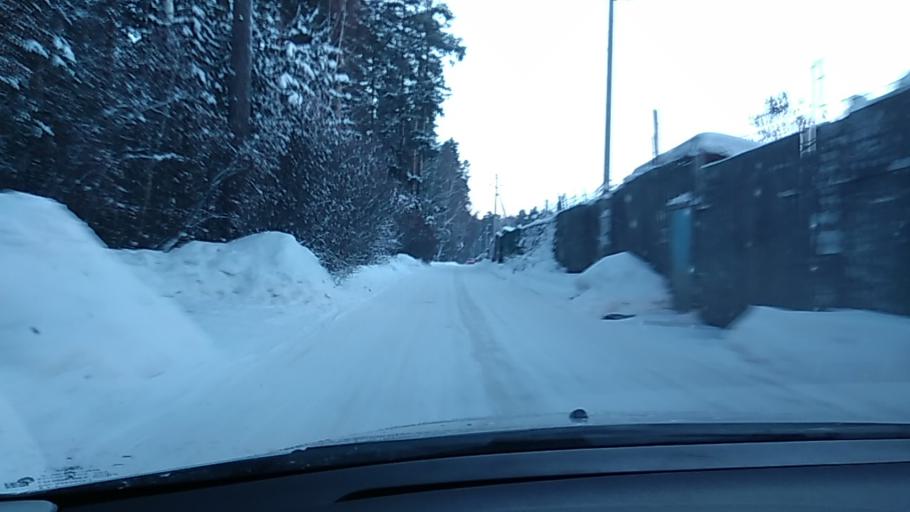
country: RU
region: Sverdlovsk
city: Verkhnyaya Pyshma
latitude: 56.9194
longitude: 60.5843
